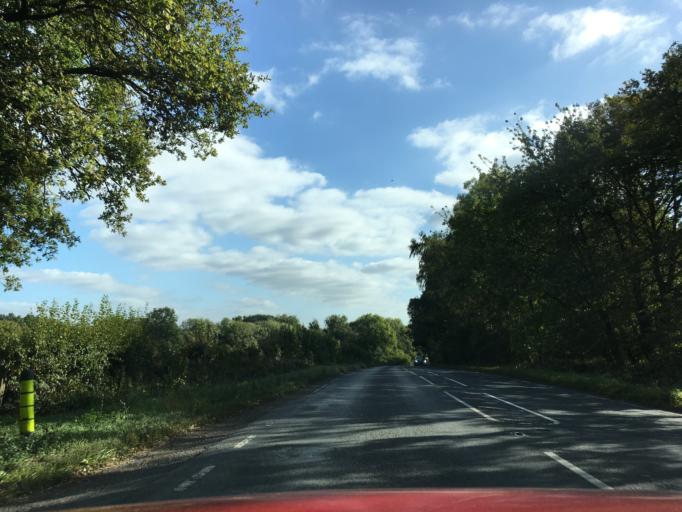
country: GB
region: England
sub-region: Hampshire
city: Tadley
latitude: 51.3139
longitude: -1.1174
